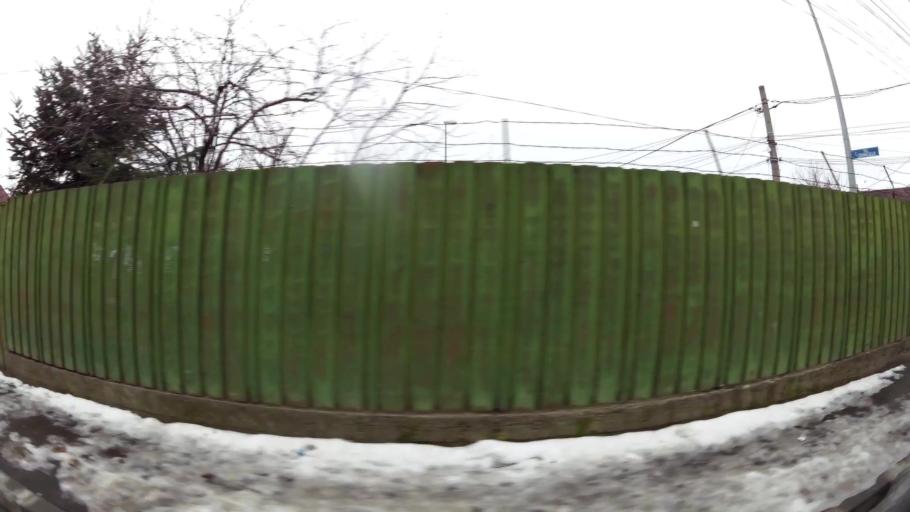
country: RO
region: Ilfov
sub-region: Comuna Pantelimon
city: Pantelimon
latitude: 44.4603
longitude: 26.2051
